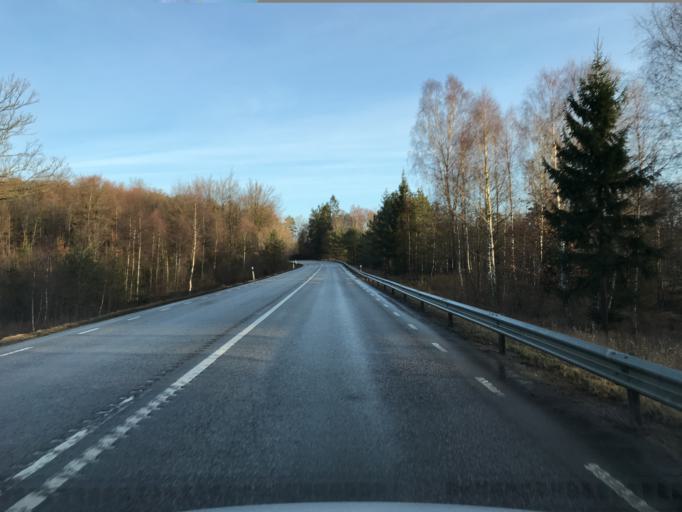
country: SE
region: Skane
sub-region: Hassleholms Kommun
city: Bjarnum
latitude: 56.2643
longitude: 13.7197
